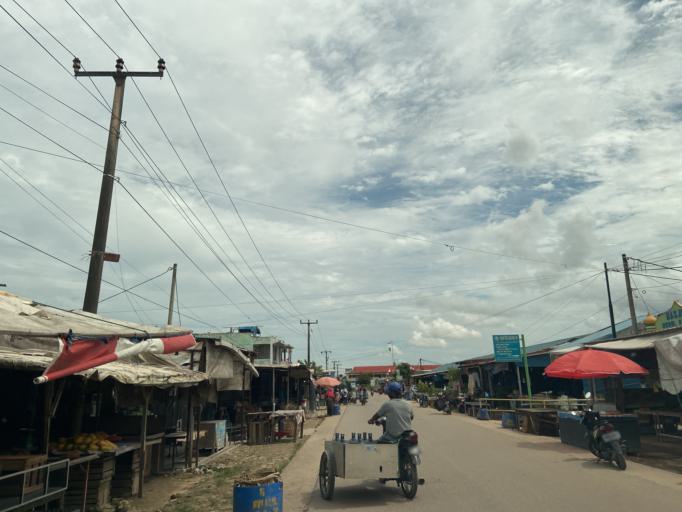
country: SG
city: Singapore
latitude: 1.0315
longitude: 103.9760
